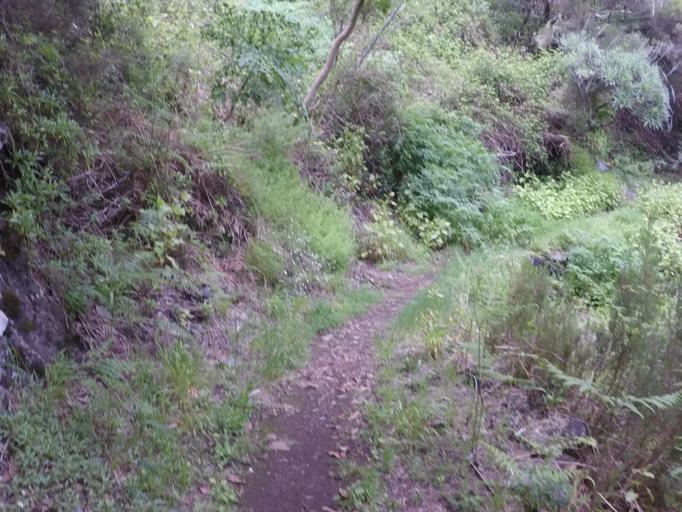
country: PT
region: Madeira
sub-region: Camara de Lobos
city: Curral das Freiras
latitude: 32.7364
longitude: -16.9933
